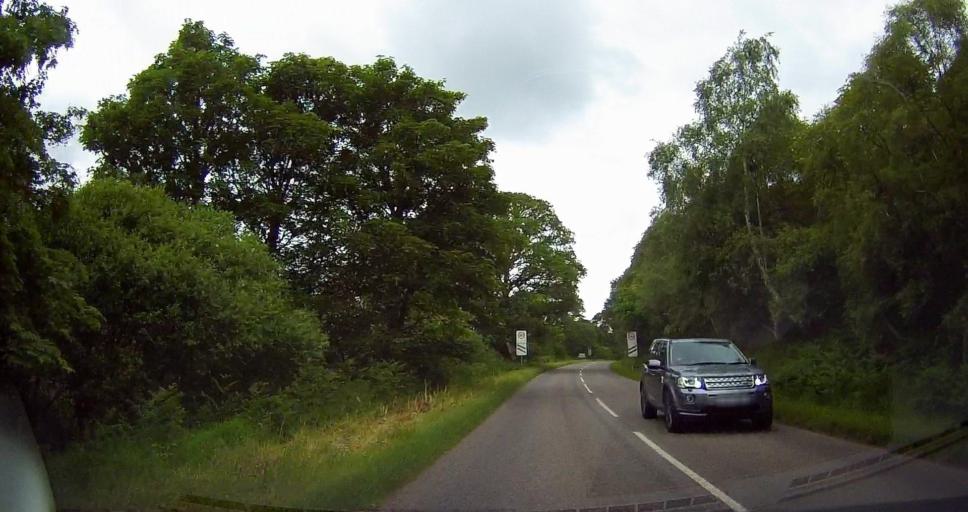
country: GB
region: Scotland
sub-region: Highland
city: Dornoch
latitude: 57.9847
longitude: -4.1486
